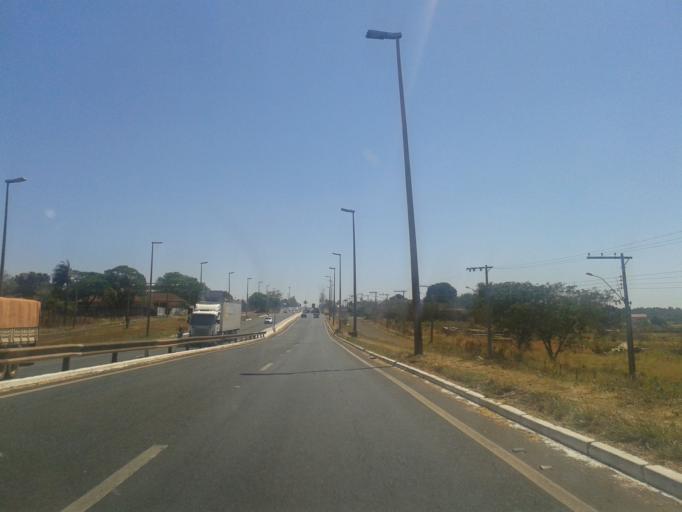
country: BR
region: Minas Gerais
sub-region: Uberlandia
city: Uberlandia
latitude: -18.9099
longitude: -48.3068
